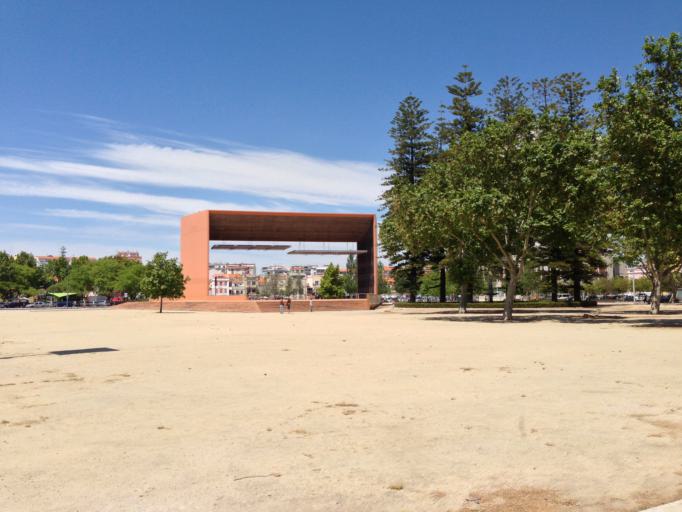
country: PT
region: Setubal
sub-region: Setubal
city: Setubal
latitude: 38.5212
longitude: -8.8982
